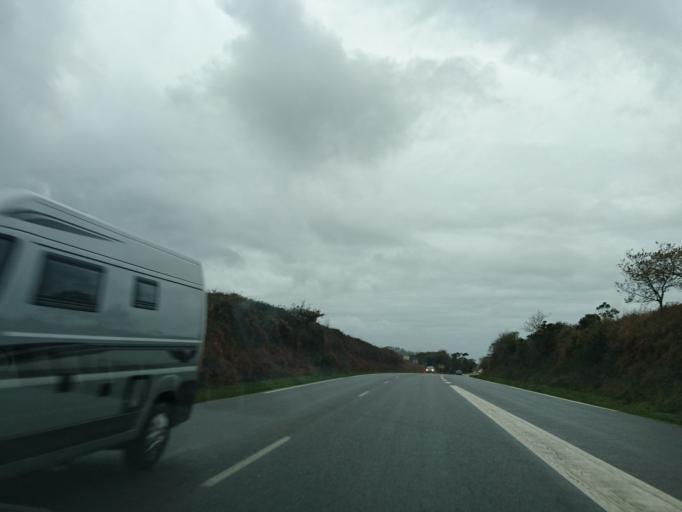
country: FR
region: Brittany
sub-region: Departement du Finistere
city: Plouzane
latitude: 48.3601
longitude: -4.6460
